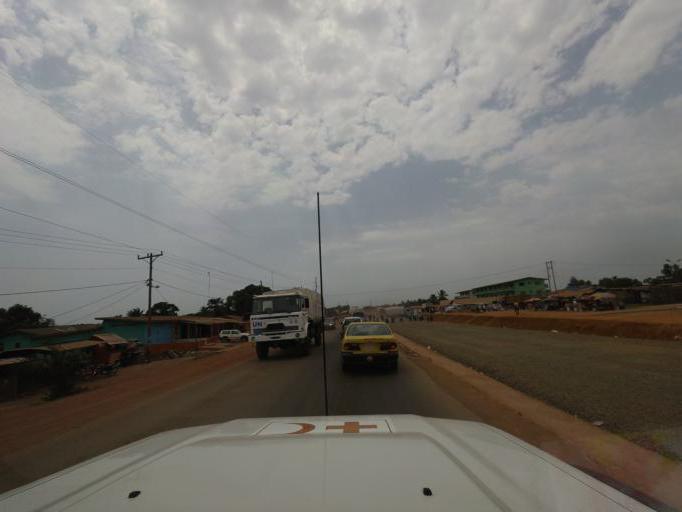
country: LR
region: Montserrado
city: Monrovia
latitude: 6.3004
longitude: -10.7052
